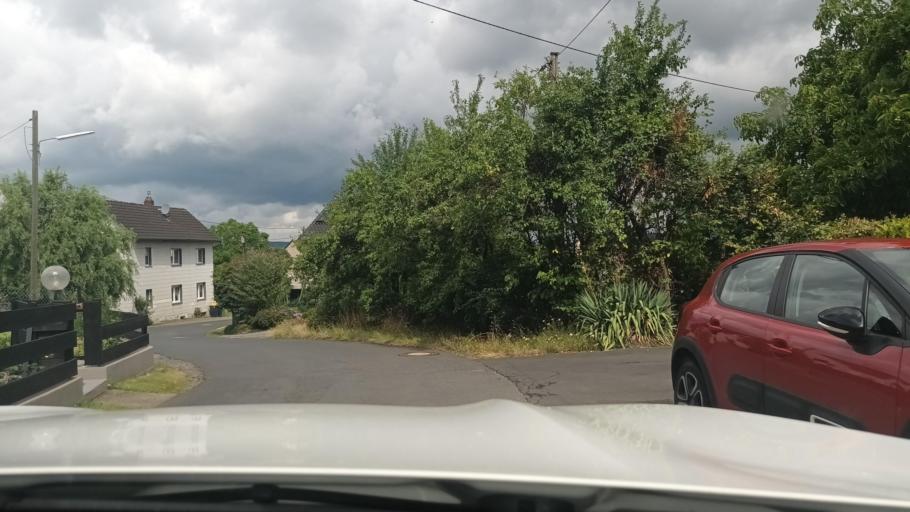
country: DE
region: North Rhine-Westphalia
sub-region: Regierungsbezirk Koln
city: Eitorf
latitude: 50.7515
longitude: 7.4552
